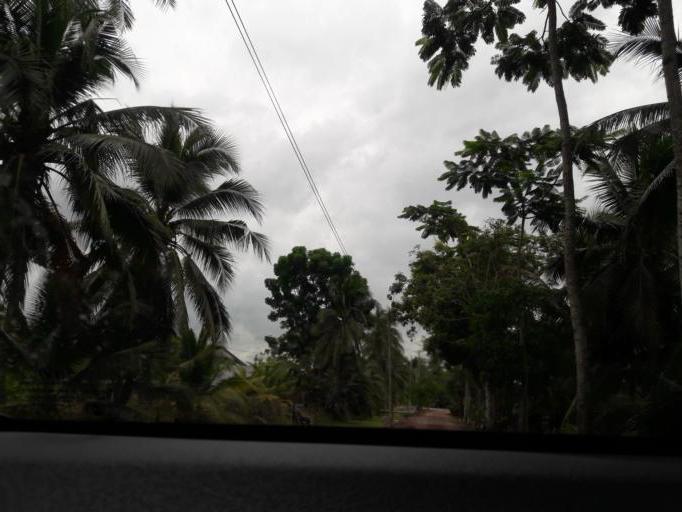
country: TH
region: Ratchaburi
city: Damnoen Saduak
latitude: 13.5739
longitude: 99.9883
